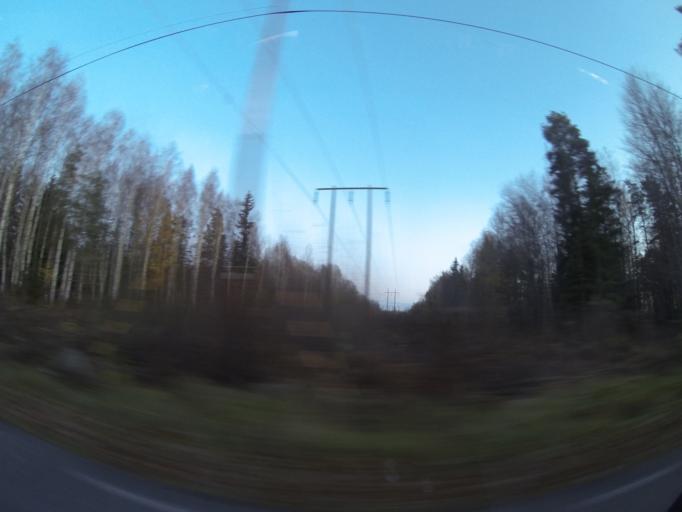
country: SE
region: OErebro
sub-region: Lindesbergs Kommun
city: Frovi
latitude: 59.3205
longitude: 15.4164
